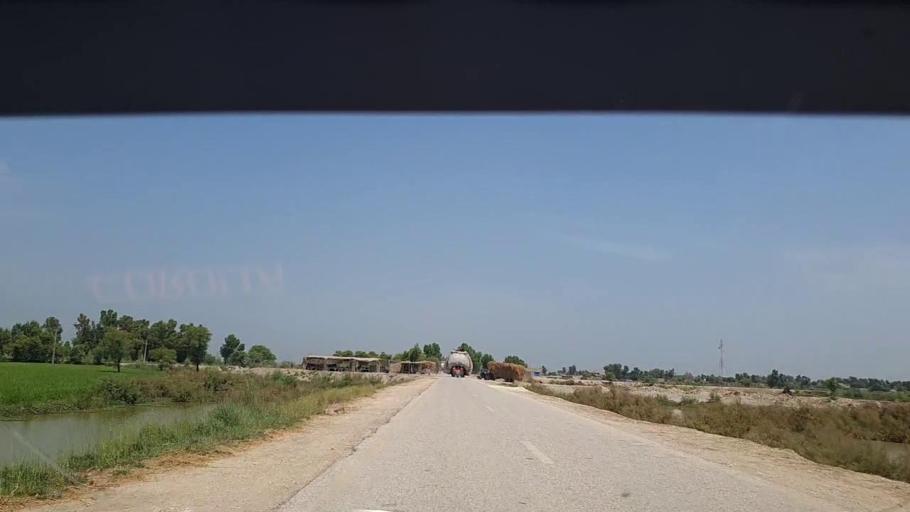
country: PK
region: Sindh
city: Thul
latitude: 28.1152
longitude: 68.8106
